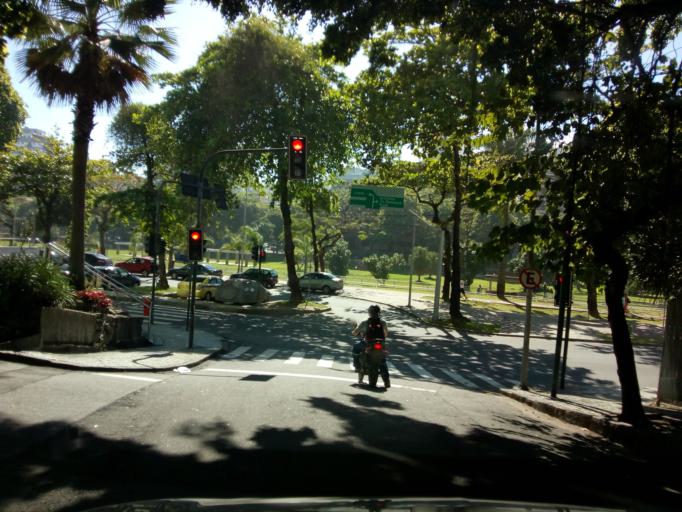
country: BR
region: Rio de Janeiro
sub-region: Rio De Janeiro
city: Rio de Janeiro
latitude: -22.9830
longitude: -43.2160
